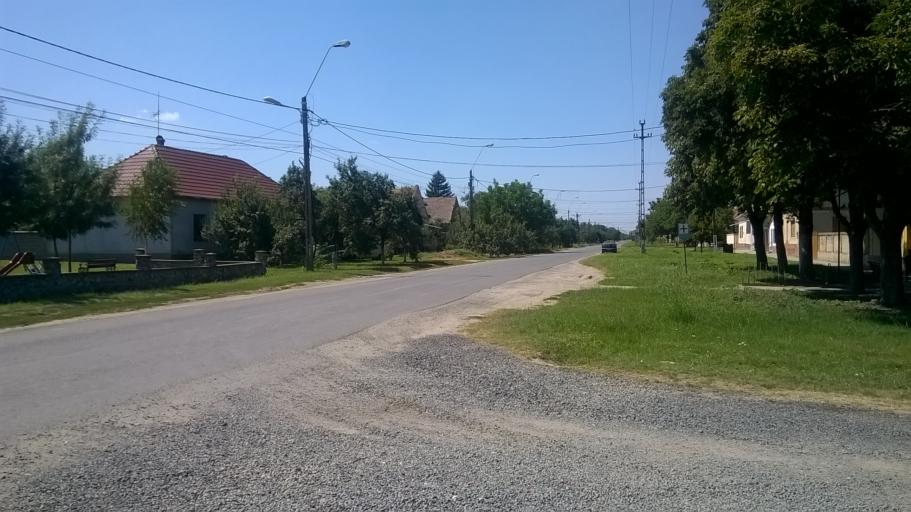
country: RO
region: Timis
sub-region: Comuna Dudestii Vechi
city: Dudestii Vechi
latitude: 46.0428
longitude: 20.4744
